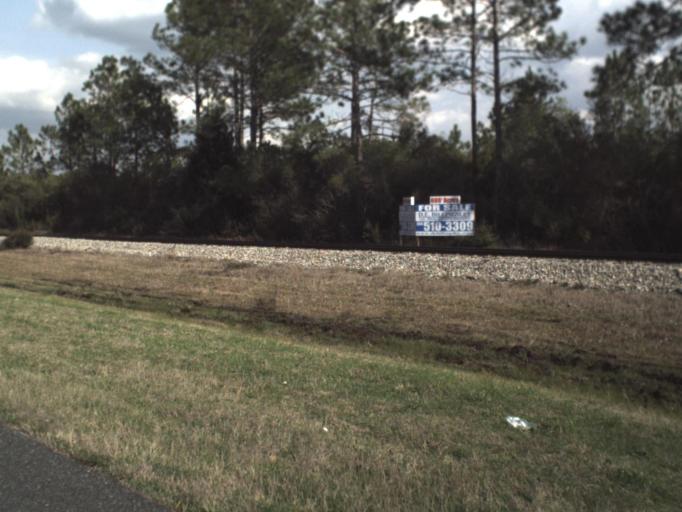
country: US
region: Florida
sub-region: Bay County
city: Youngstown
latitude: 30.3020
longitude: -85.4818
